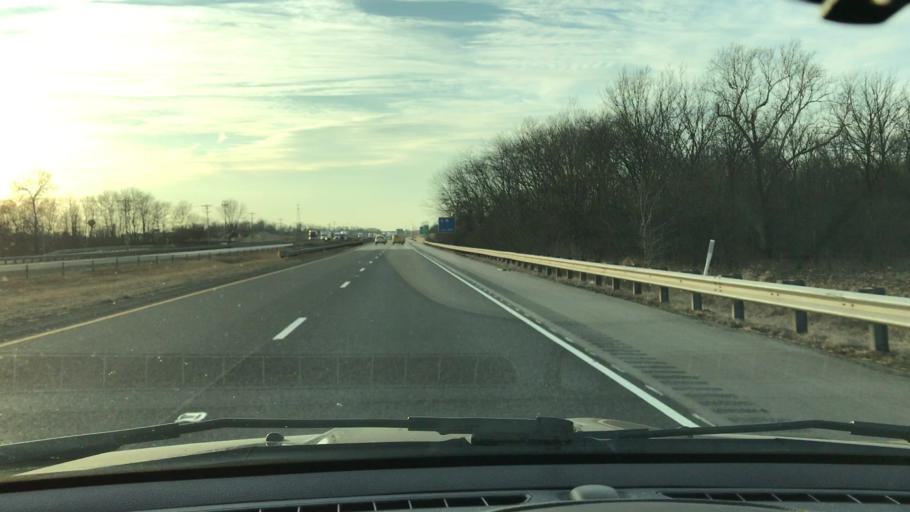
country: US
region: Indiana
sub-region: Wayne County
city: Cambridge City
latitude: 39.8530
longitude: -85.1322
